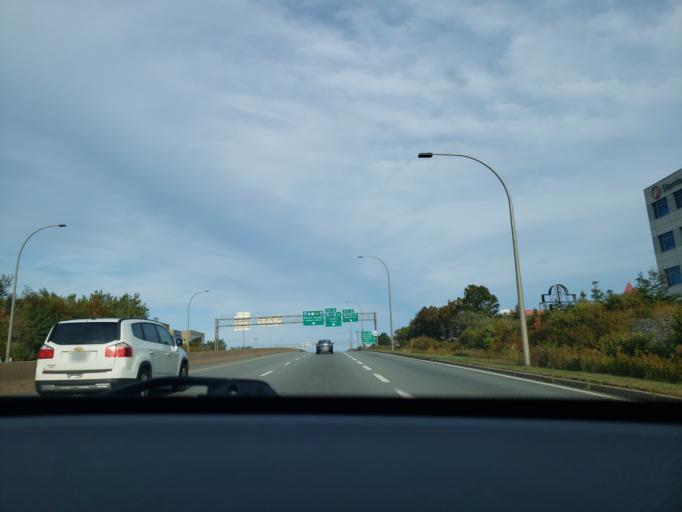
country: CA
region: Nova Scotia
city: Dartmouth
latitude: 44.6904
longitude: -63.5889
